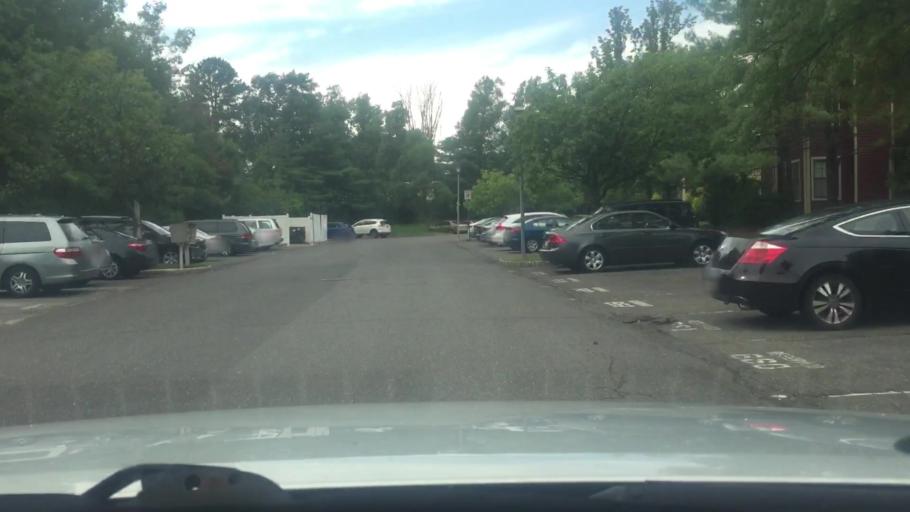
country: US
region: New Jersey
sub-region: Middlesex County
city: South River
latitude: 40.4572
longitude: -74.4059
